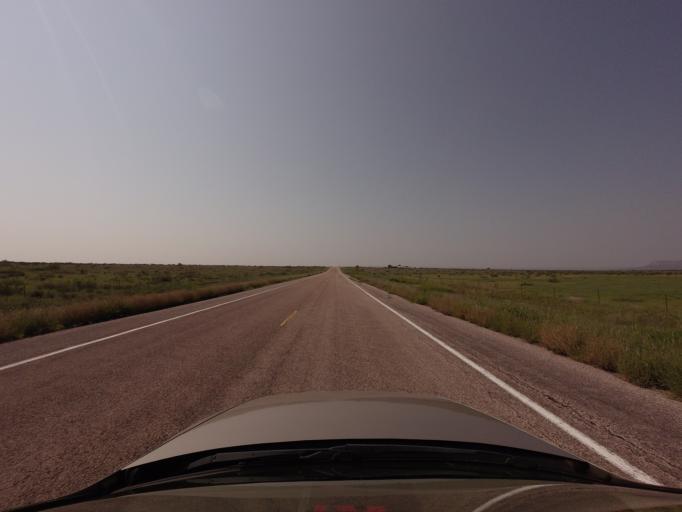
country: US
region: New Mexico
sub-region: Quay County
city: Tucumcari
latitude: 34.9604
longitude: -103.7565
